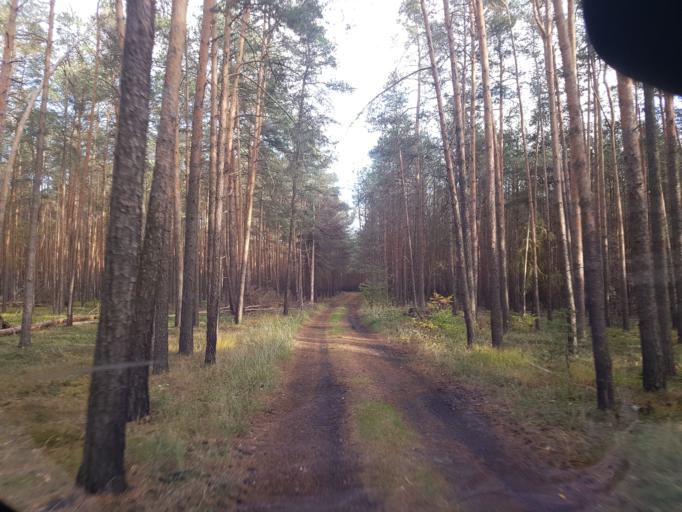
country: DE
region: Brandenburg
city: Finsterwalde
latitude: 51.5538
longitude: 13.6849
